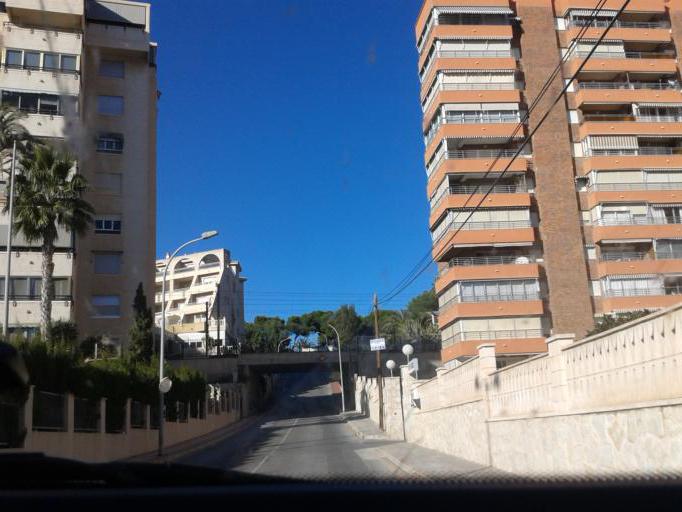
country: ES
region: Valencia
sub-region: Provincia de Alicante
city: el Campello
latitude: 38.4140
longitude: -0.3988
